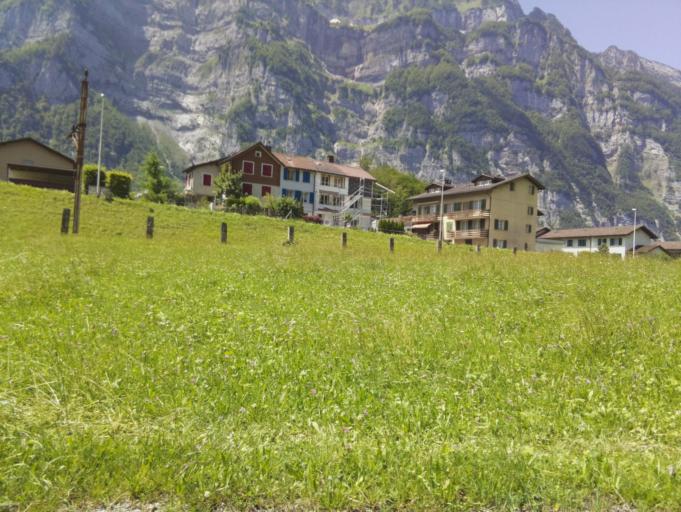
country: CH
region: Glarus
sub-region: Glarus
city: Netstal
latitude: 47.0580
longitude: 9.0601
